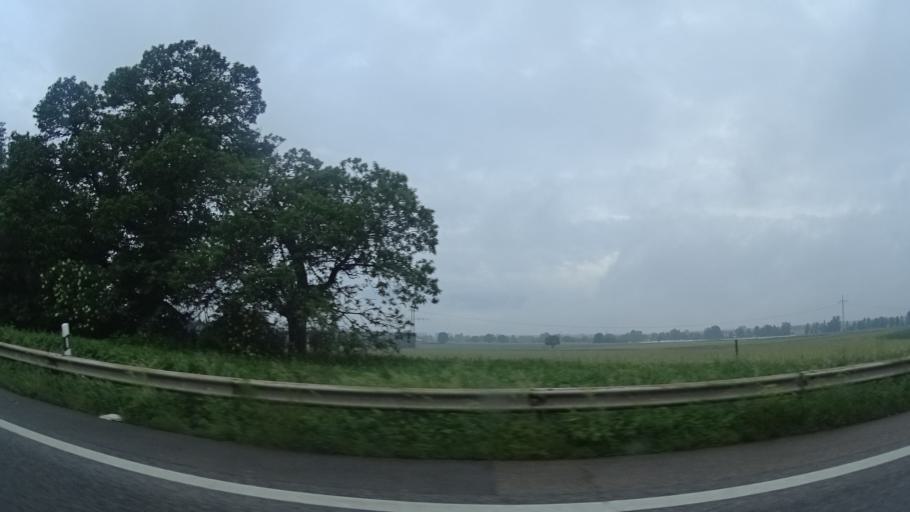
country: DE
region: Rheinland-Pfalz
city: Dudenhofen
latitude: 49.3047
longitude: 8.4059
